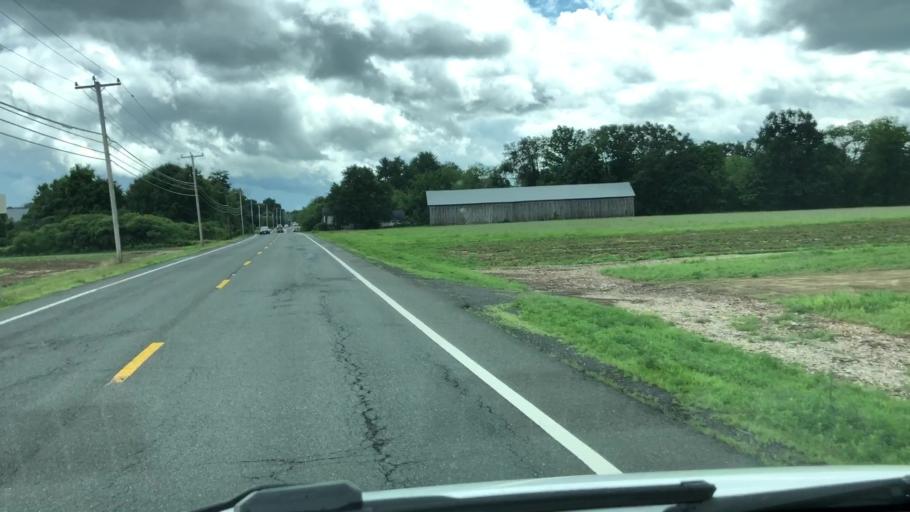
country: US
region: Massachusetts
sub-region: Franklin County
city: Whately
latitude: 42.4423
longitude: -72.6253
